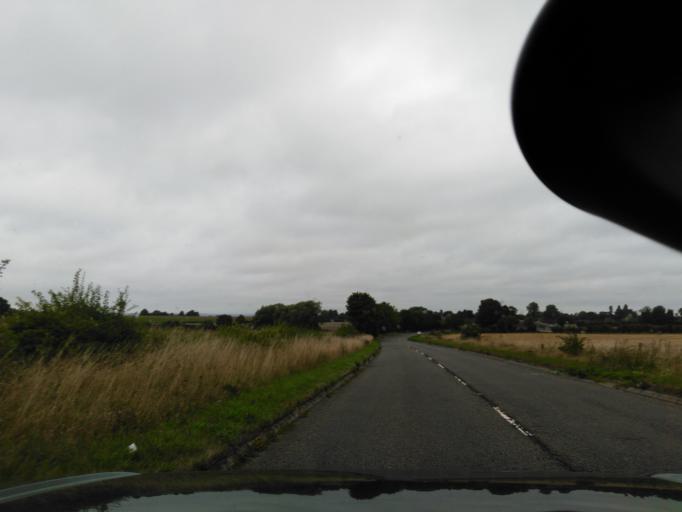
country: GB
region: England
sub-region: Wiltshire
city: Upton Scudamore
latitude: 51.2411
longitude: -2.1884
